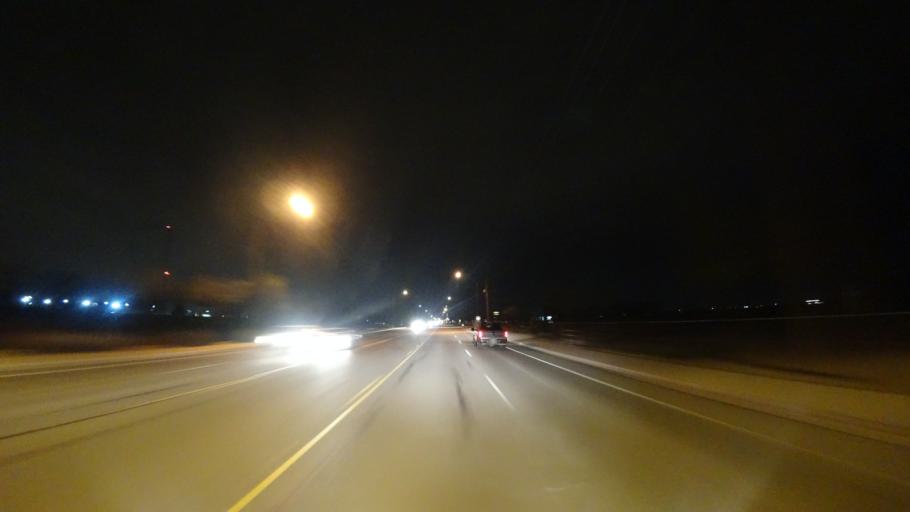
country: US
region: Arizona
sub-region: Maricopa County
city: Gilbert
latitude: 33.2698
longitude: -111.7379
